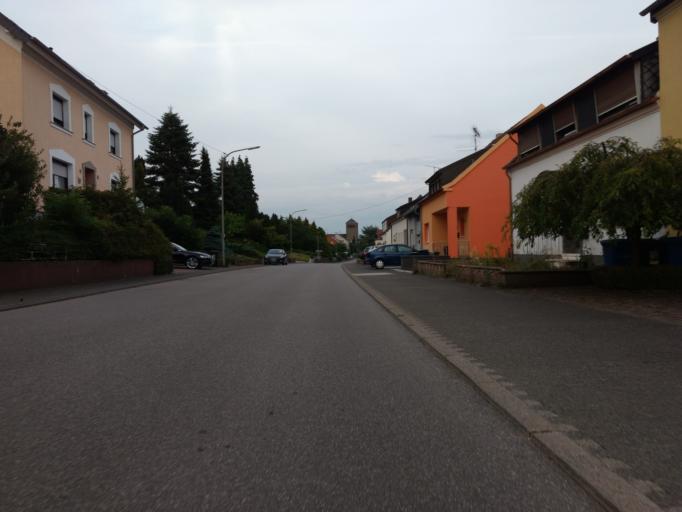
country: DE
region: Saarland
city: Rehlingen-Siersburg
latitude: 49.3312
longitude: 6.6796
